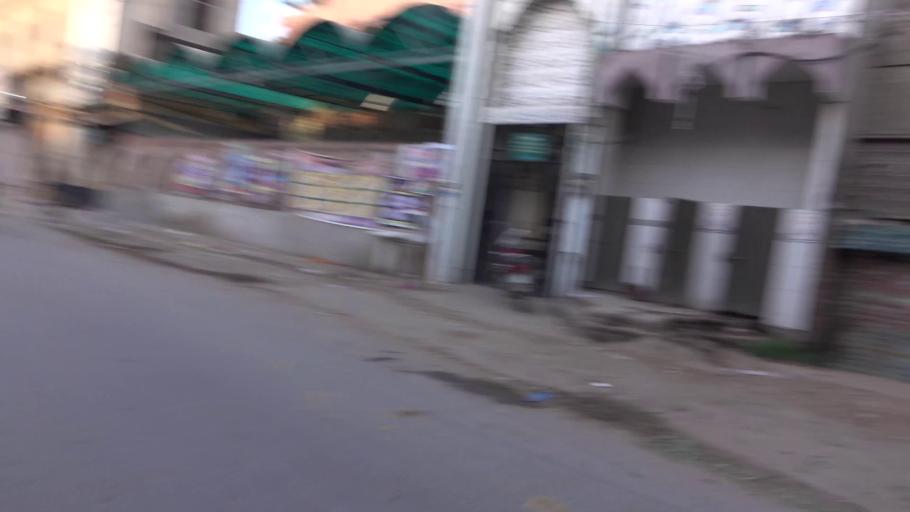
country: PK
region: Punjab
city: Hafizabad
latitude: 32.0694
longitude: 73.6891
